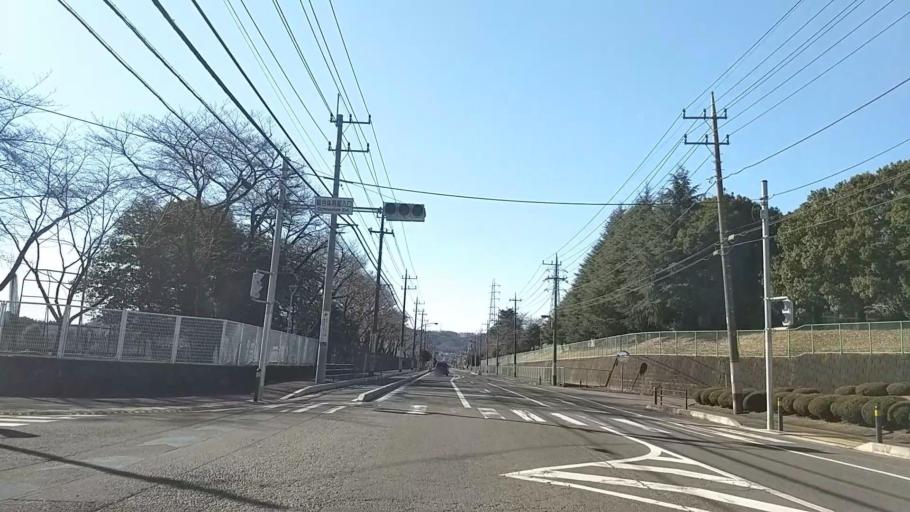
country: JP
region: Kanagawa
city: Hadano
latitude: 35.3800
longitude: 139.1963
